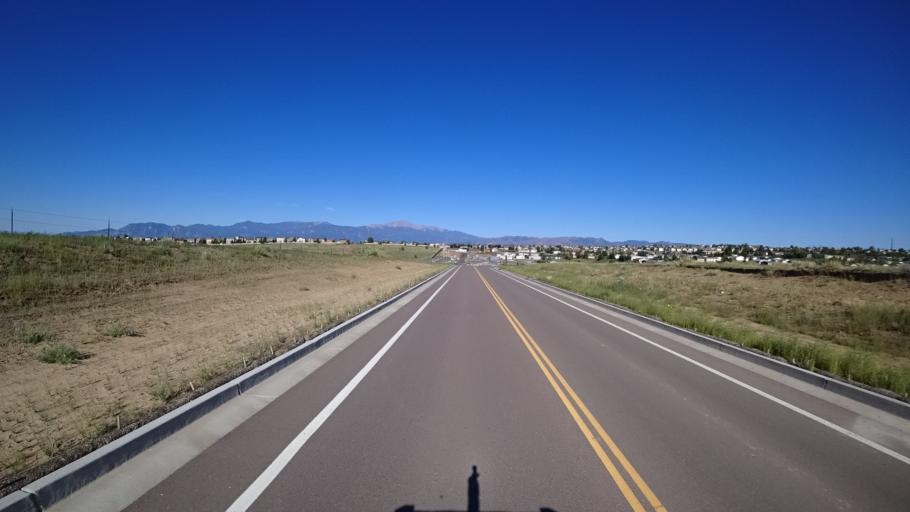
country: US
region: Colorado
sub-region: El Paso County
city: Cimarron Hills
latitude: 38.8938
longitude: -104.6810
